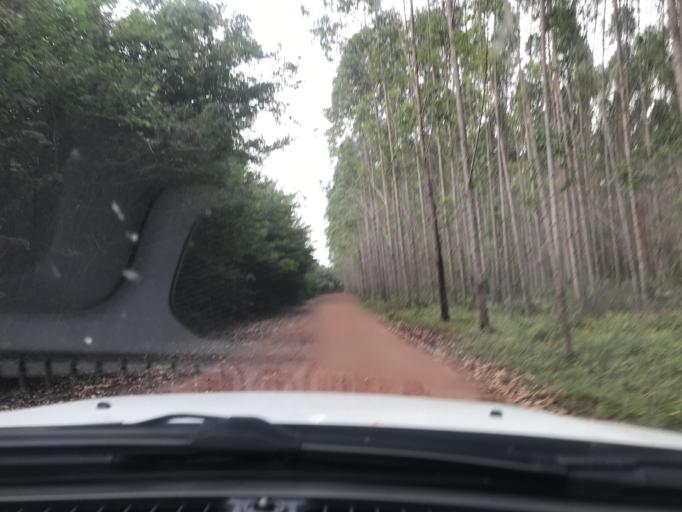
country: BR
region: Bahia
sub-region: Entre Rios
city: Entre Rios
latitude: -12.1070
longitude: -38.1862
